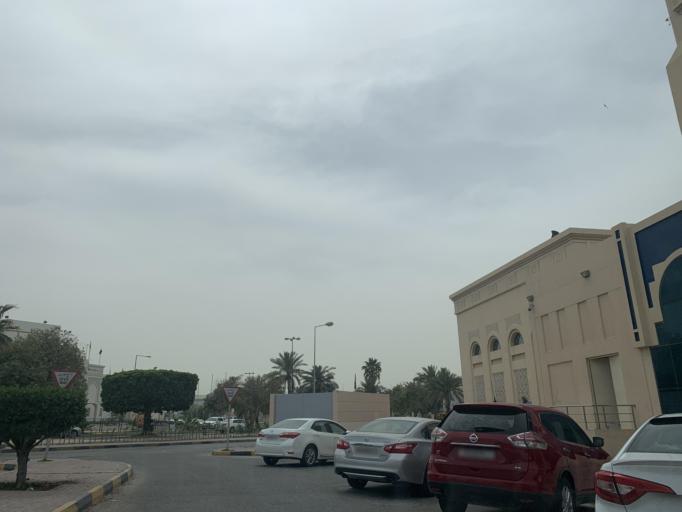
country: BH
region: Northern
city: Madinat `Isa
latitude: 26.1712
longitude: 50.5472
